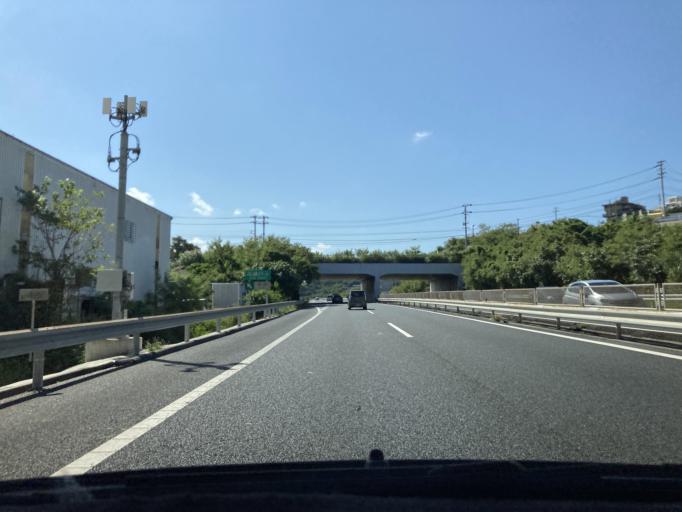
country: JP
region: Okinawa
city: Ginowan
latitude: 26.2411
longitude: 127.7430
